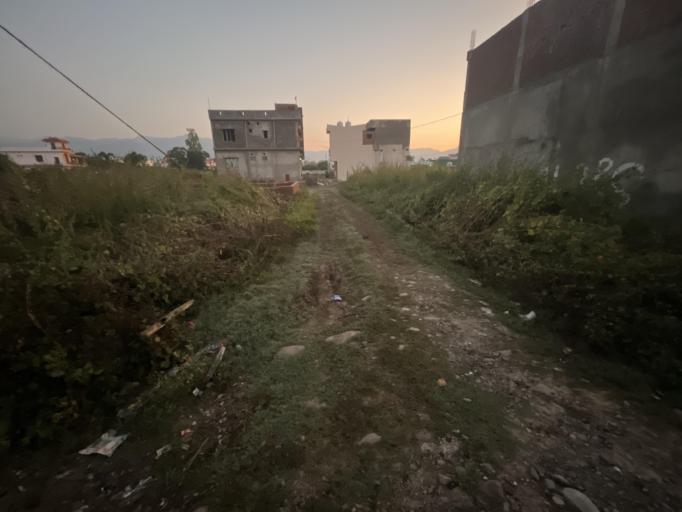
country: IN
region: Uttarakhand
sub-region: Naini Tal
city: Haldwani
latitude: 29.1983
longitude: 79.4844
